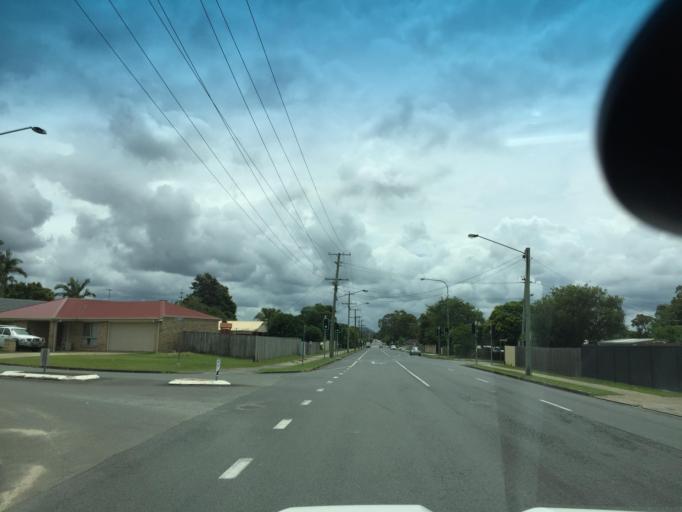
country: AU
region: Queensland
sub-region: Moreton Bay
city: Caboolture
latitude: -27.0772
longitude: 152.9319
